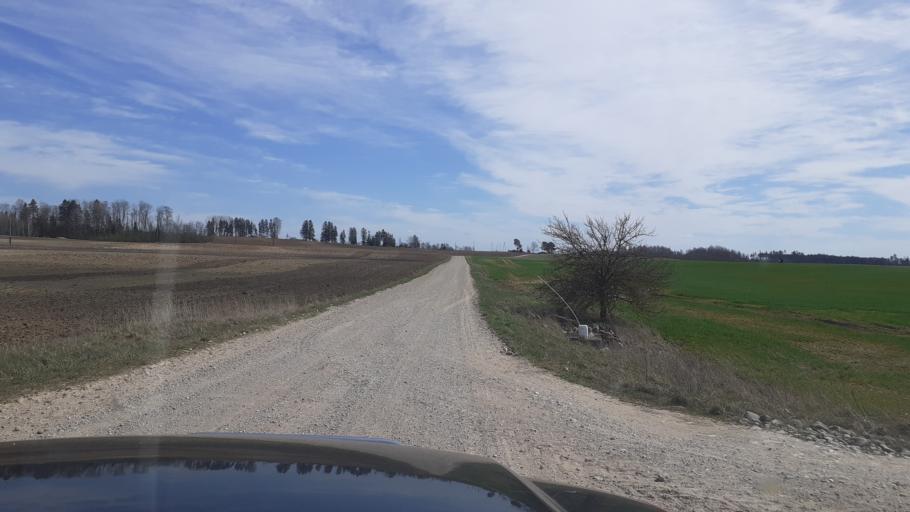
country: LV
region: Kuldigas Rajons
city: Kuldiga
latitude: 56.8430
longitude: 21.9826
